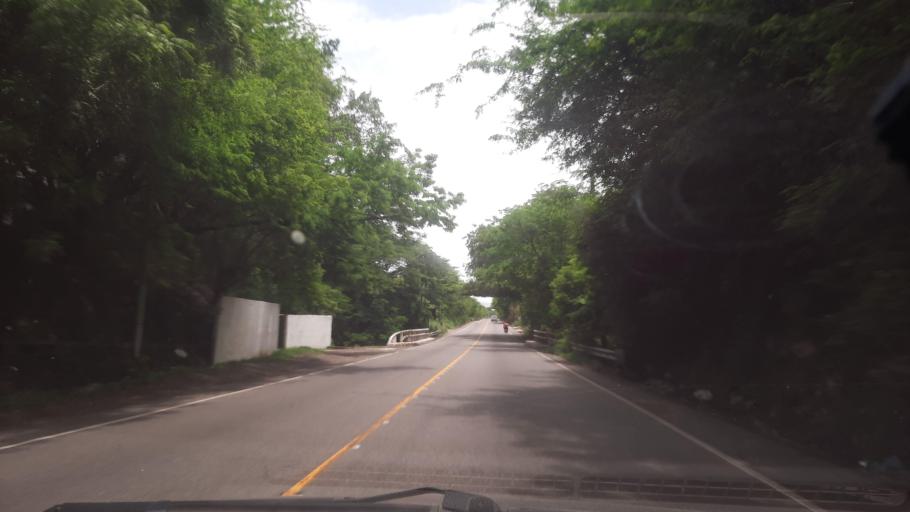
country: GT
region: Zacapa
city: Rio Hondo
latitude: 15.0626
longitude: -89.5340
